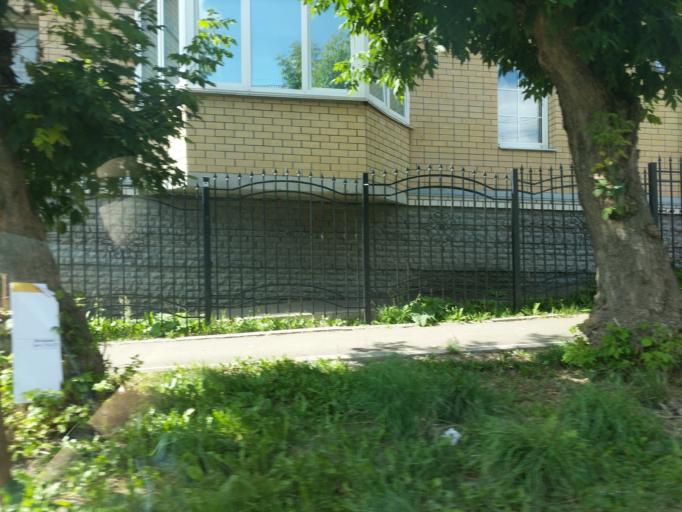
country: RU
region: Kirov
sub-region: Kirovo-Chepetskiy Rayon
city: Kirov
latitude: 58.6000
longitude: 49.6770
